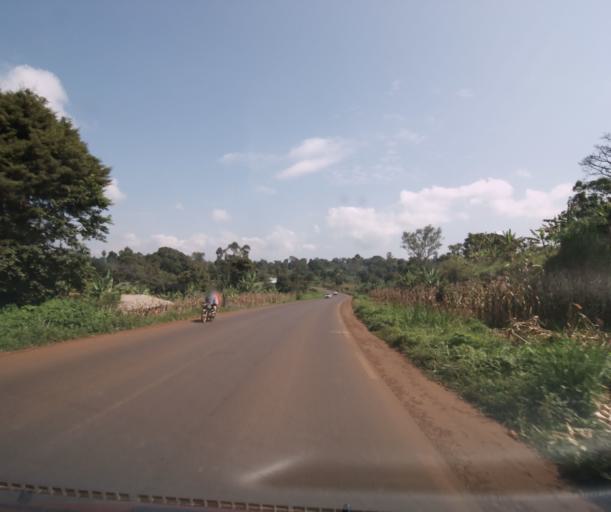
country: CM
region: West
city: Bansoa
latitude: 5.4897
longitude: 10.2648
